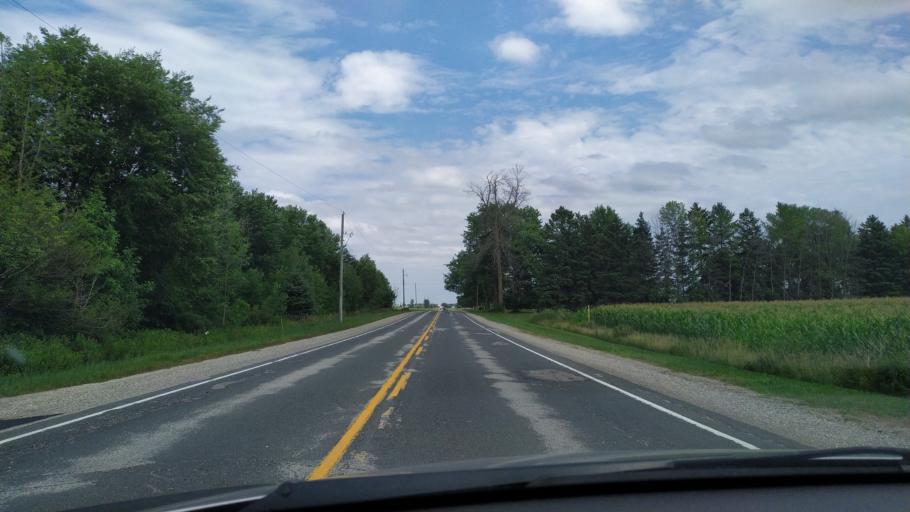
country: CA
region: Ontario
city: Stratford
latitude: 43.3523
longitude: -80.9327
